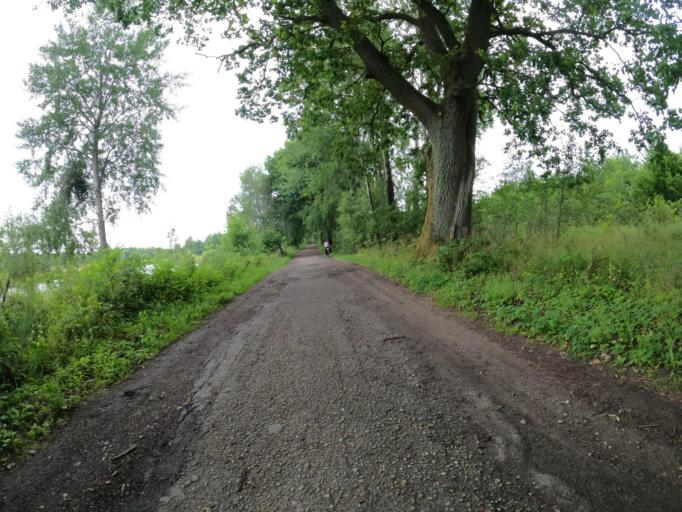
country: PL
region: West Pomeranian Voivodeship
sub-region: Powiat szczecinecki
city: Grzmiaca
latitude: 53.9576
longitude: 16.4598
